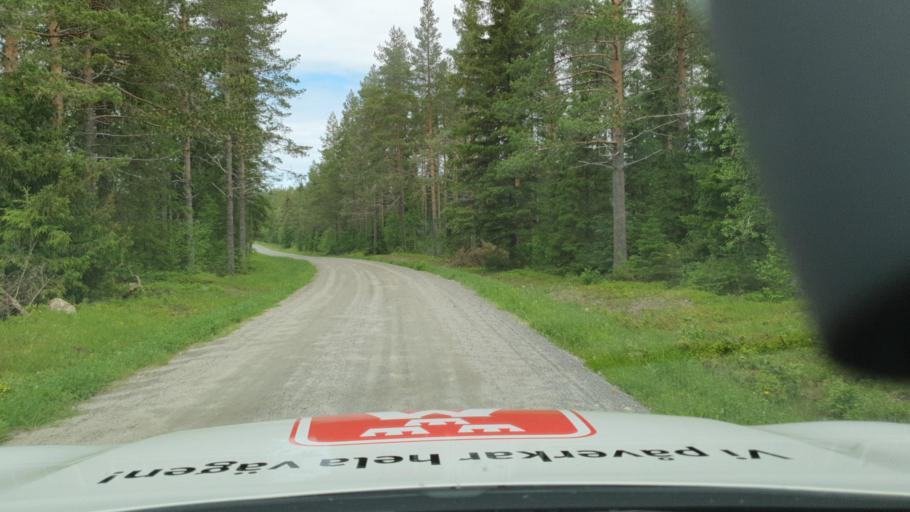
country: SE
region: Vaesterbotten
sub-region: Skelleftea Kommun
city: Langsele
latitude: 64.4824
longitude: 20.2588
